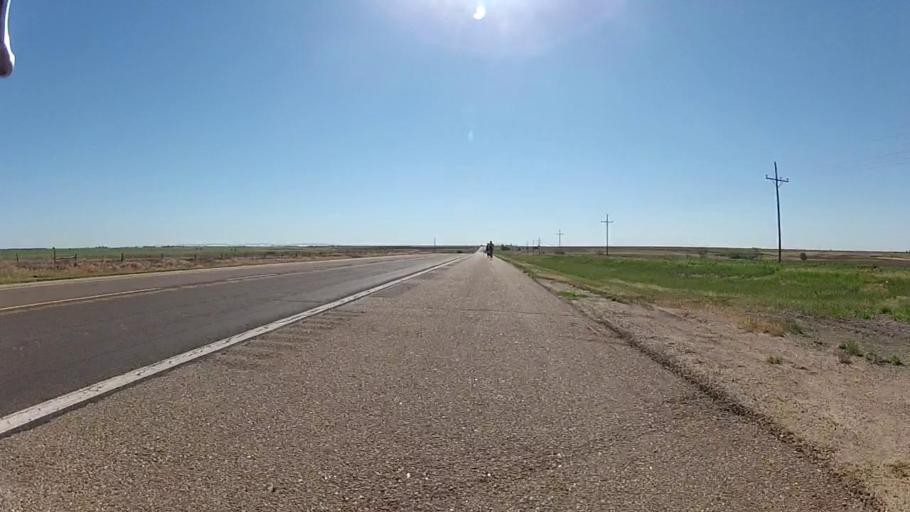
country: US
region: Kansas
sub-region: Kiowa County
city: Greensburg
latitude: 37.5861
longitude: -99.5489
